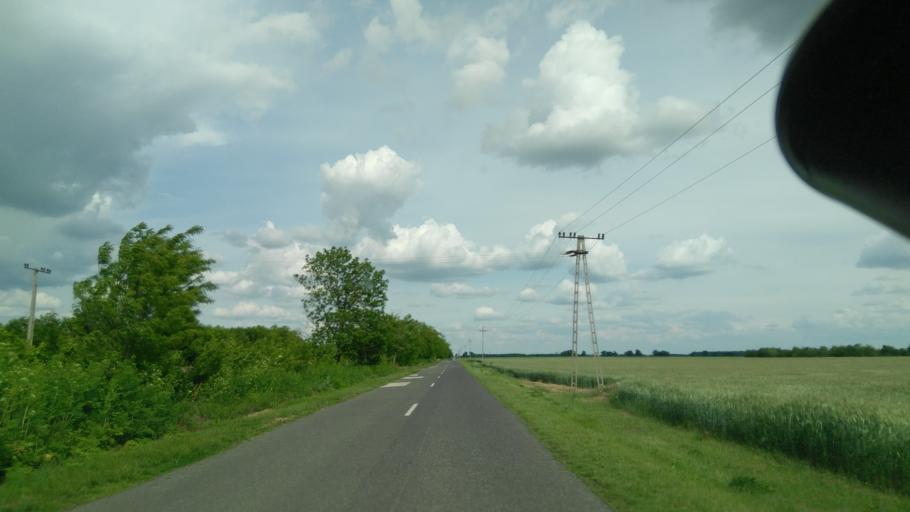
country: HU
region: Bekes
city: Mezohegyes
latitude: 46.3079
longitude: 20.8834
